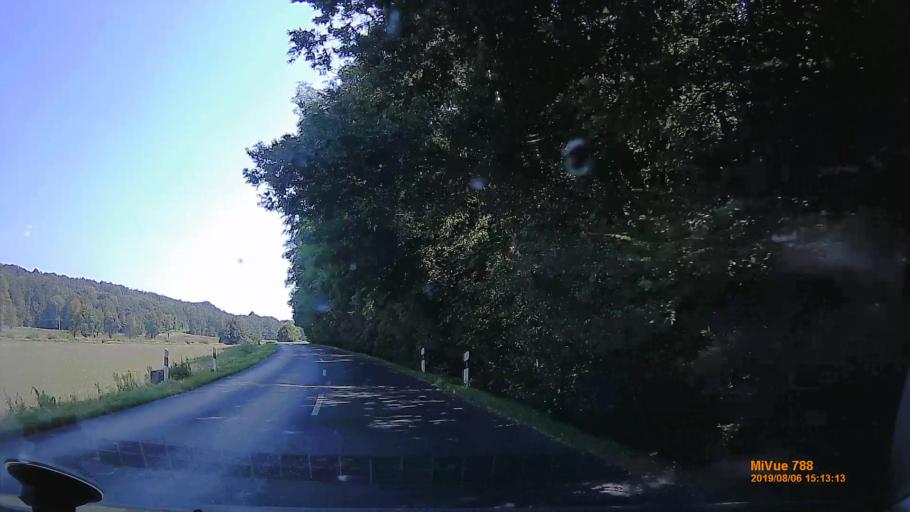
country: HU
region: Zala
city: Murakeresztur
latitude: 46.3572
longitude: 16.9775
